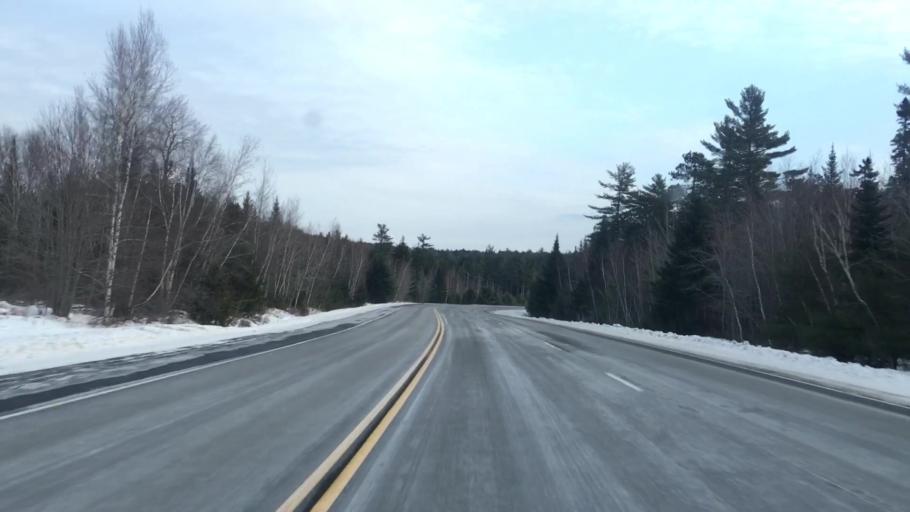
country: US
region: Maine
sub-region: Washington County
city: Addison
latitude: 44.9150
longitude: -67.7904
